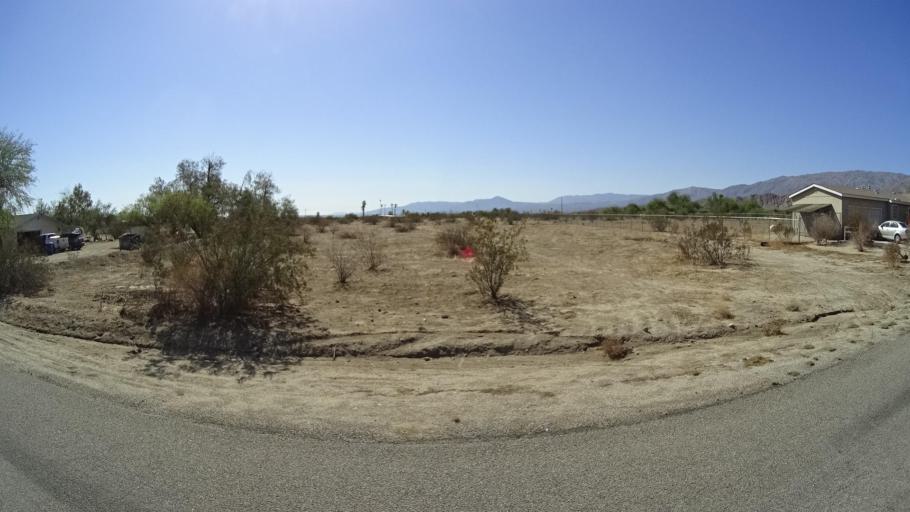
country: US
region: California
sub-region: San Diego County
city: Borrego Springs
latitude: 33.2729
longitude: -116.3893
